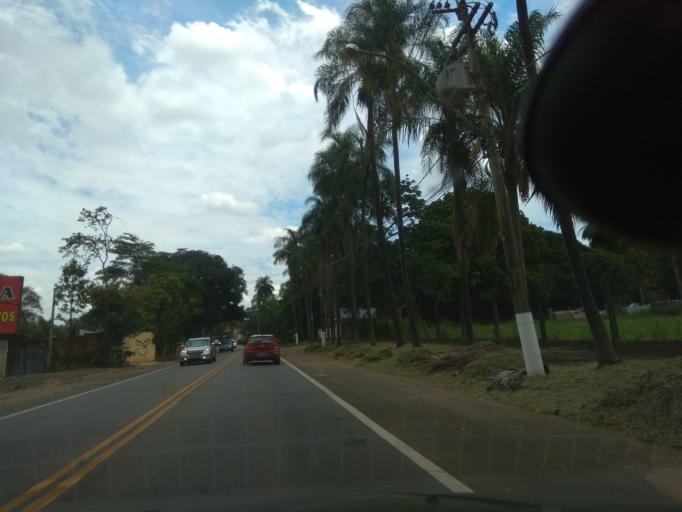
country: BR
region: Sao Paulo
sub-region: Paulinia
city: Paulinia
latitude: -22.8156
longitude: -47.0808
